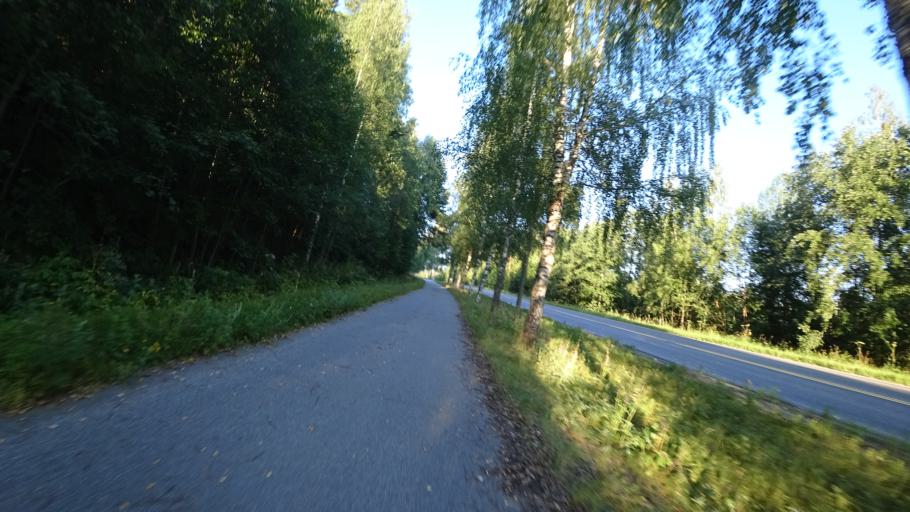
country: FI
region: Pirkanmaa
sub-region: Tampere
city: Nokia
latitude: 61.4664
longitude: 23.4265
